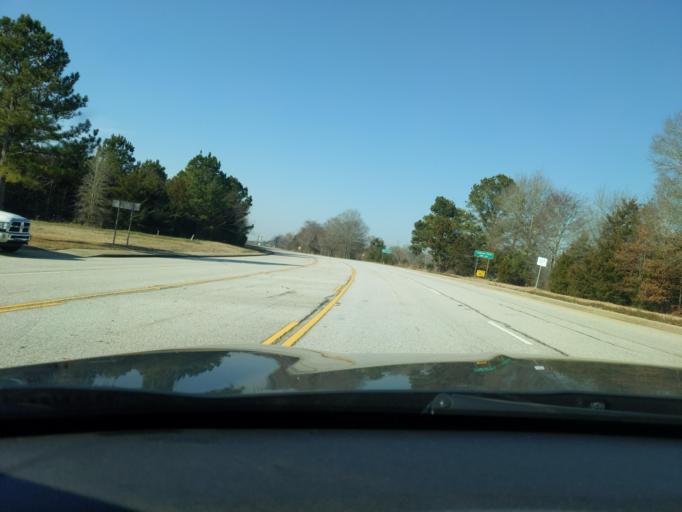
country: US
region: South Carolina
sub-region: Abbeville County
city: Calhoun Falls
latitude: 34.0973
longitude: -82.5802
